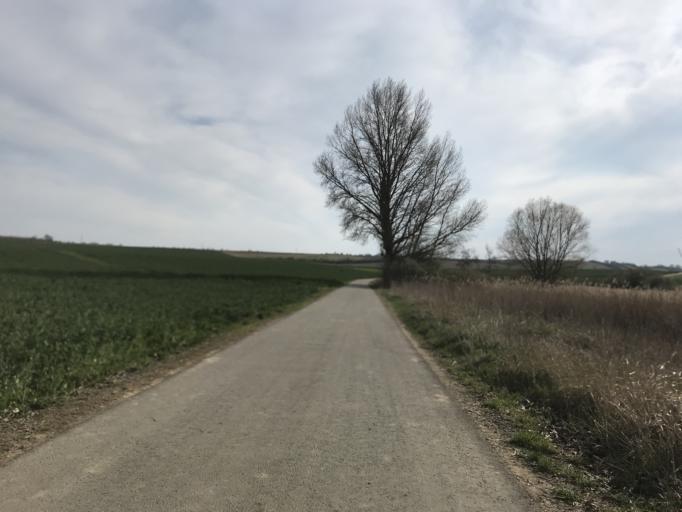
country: DE
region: Rheinland-Pfalz
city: Stadecken-Elsheim
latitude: 49.9135
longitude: 8.1135
